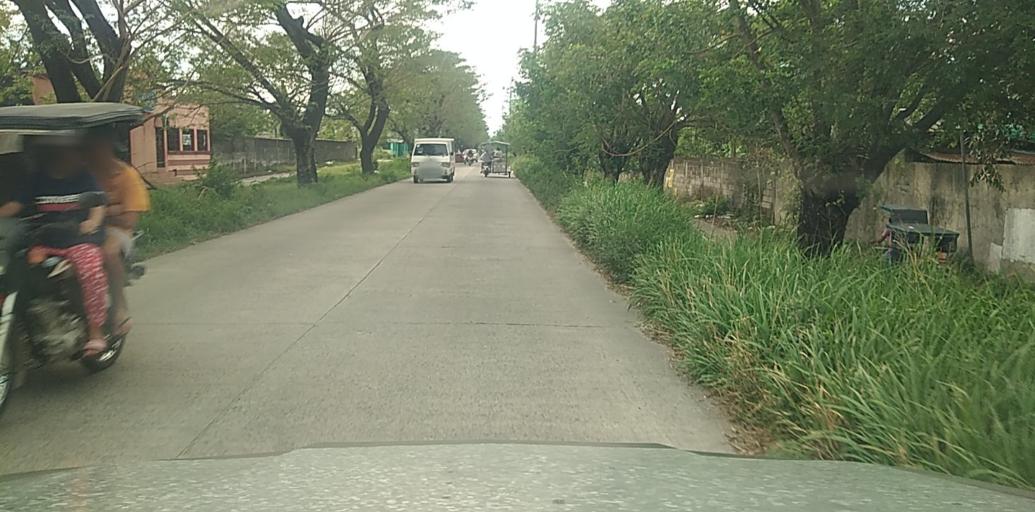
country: PH
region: Central Luzon
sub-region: Province of Pampanga
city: Pandacaqui
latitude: 15.1774
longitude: 120.6618
